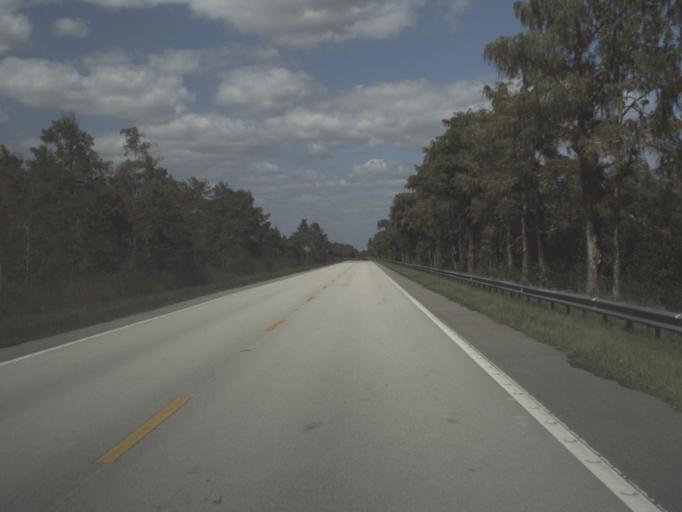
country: US
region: Florida
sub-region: Miami-Dade County
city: Kendall West
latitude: 25.8336
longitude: -80.9059
